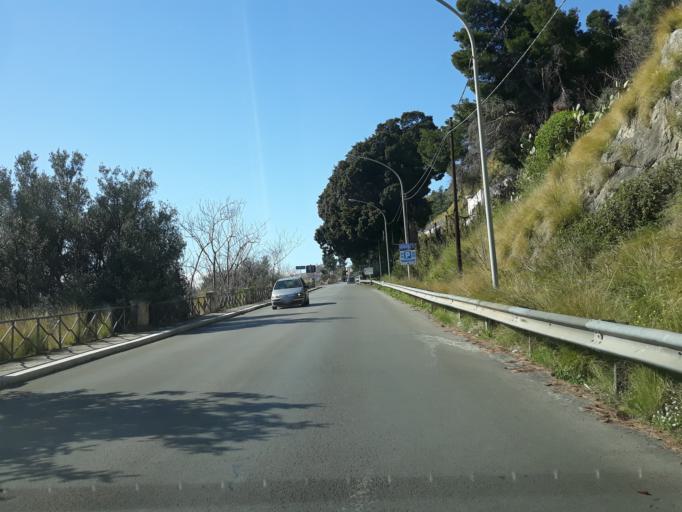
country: IT
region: Sicily
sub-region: Palermo
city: Monreale
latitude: 38.0924
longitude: 13.3039
